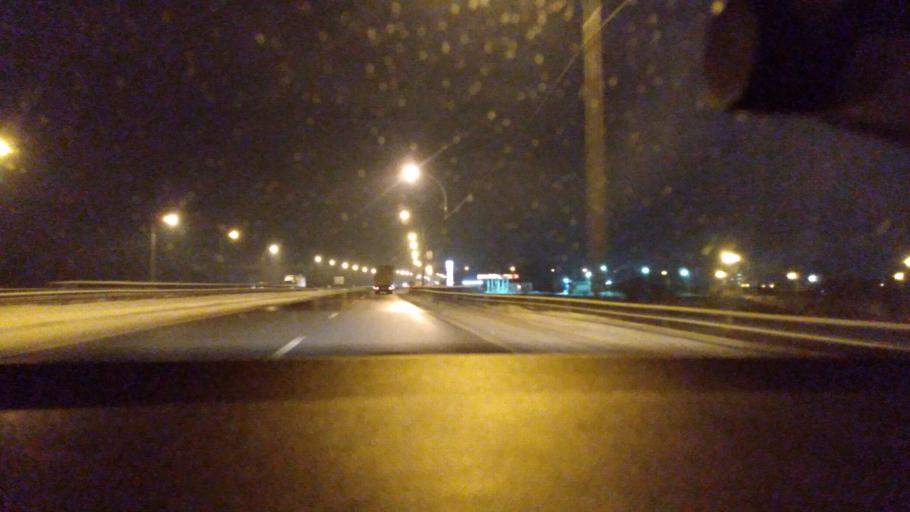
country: RU
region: Moskovskaya
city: Kolomna
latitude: 55.0898
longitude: 38.9051
